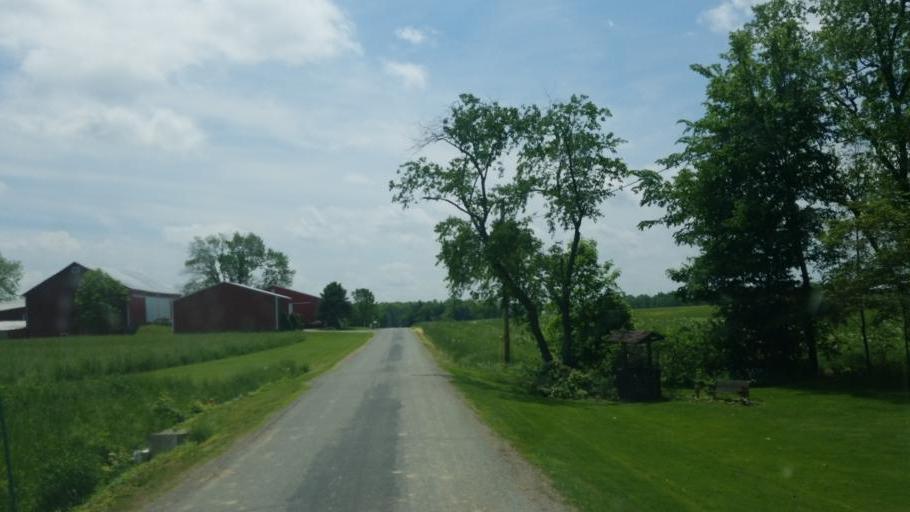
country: US
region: Ohio
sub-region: Ashland County
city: Ashland
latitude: 40.8447
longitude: -82.2267
